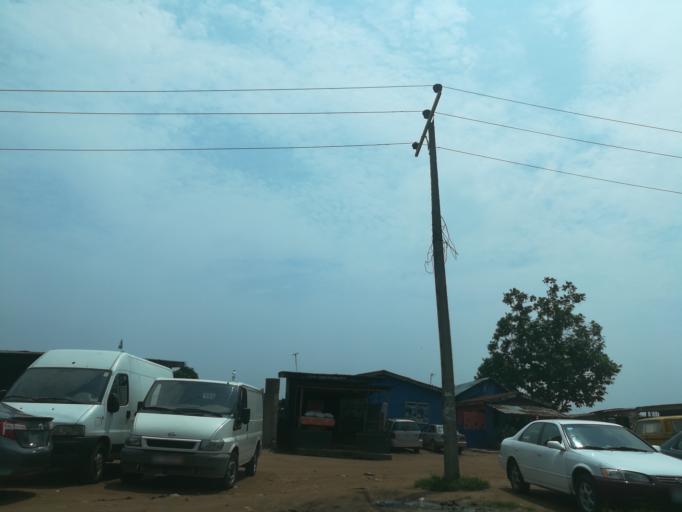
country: NG
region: Lagos
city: Ikorodu
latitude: 6.6015
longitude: 3.6229
